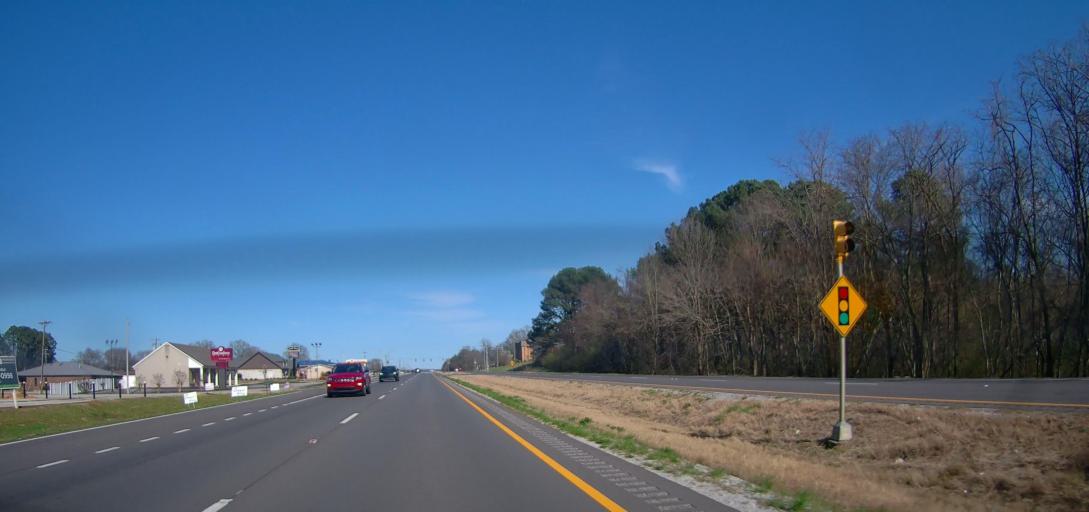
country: US
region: Alabama
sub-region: Lauderdale County
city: Killen
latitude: 34.8570
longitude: -87.5456
